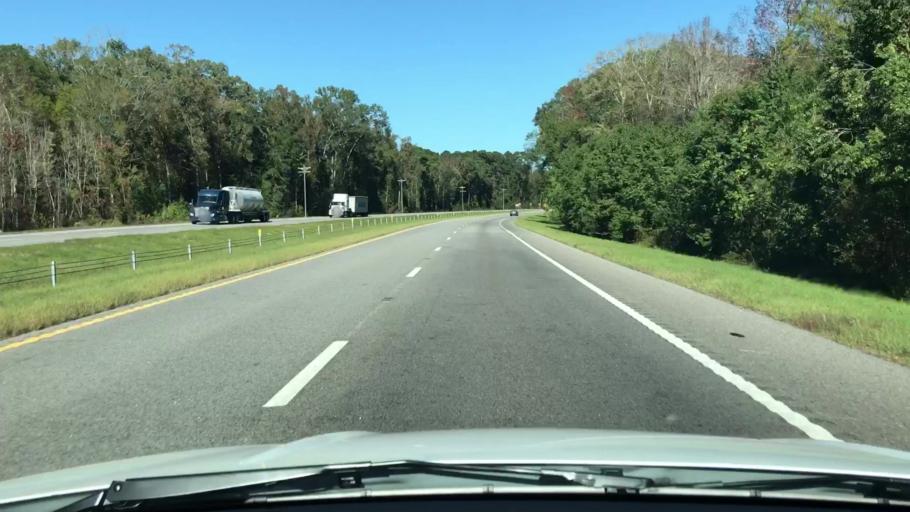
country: US
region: South Carolina
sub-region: Colleton County
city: Walterboro
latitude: 32.7267
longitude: -80.5996
